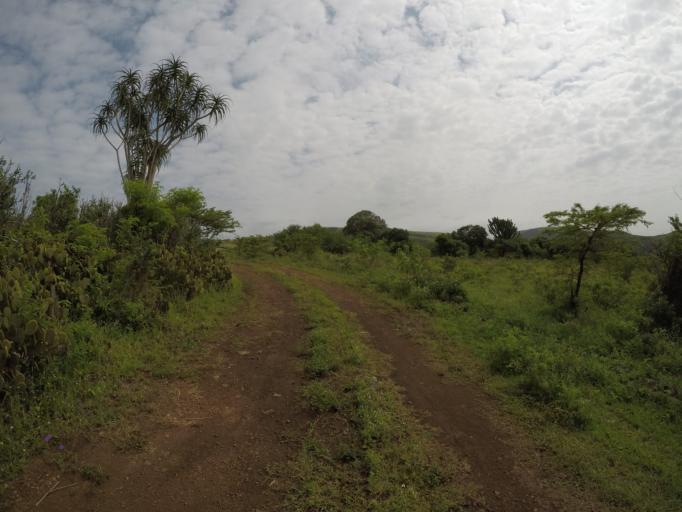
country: ZA
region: KwaZulu-Natal
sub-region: uThungulu District Municipality
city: Empangeni
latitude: -28.6218
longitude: 31.9101
